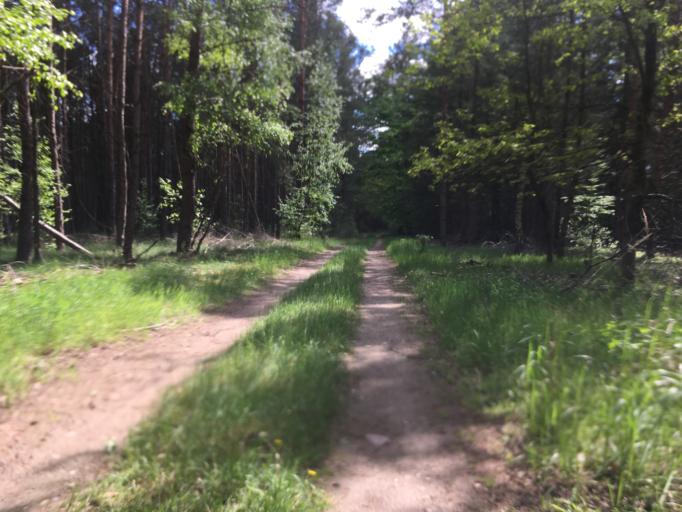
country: DE
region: Brandenburg
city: Marienwerder
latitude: 52.8265
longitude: 13.6343
